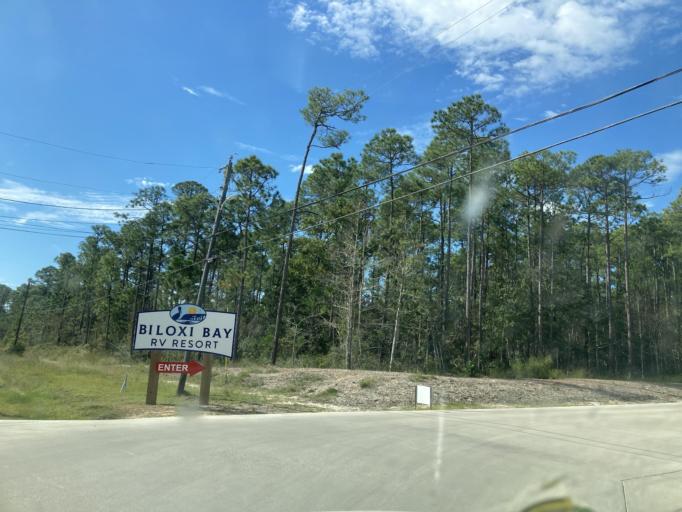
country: US
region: Mississippi
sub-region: Jackson County
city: Gulf Hills
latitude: 30.4354
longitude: -88.8540
